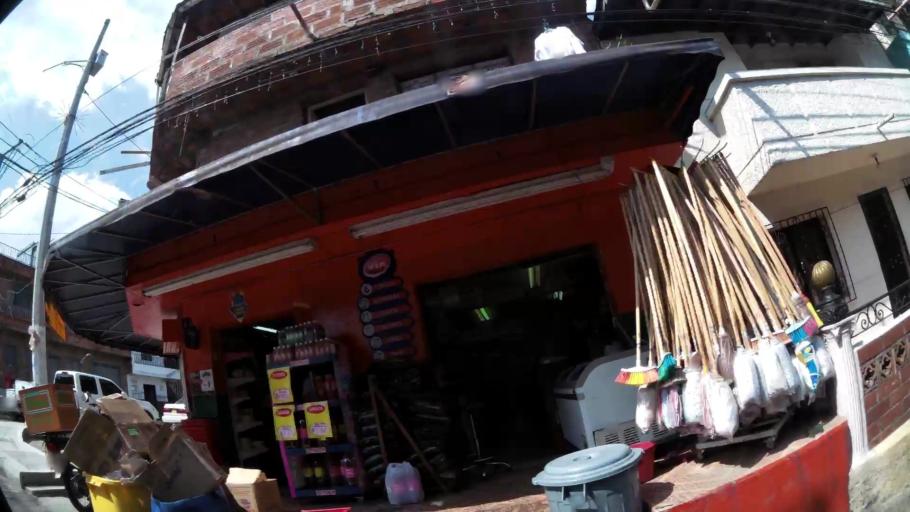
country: CO
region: Antioquia
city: Medellin
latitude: 6.2883
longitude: -75.5788
